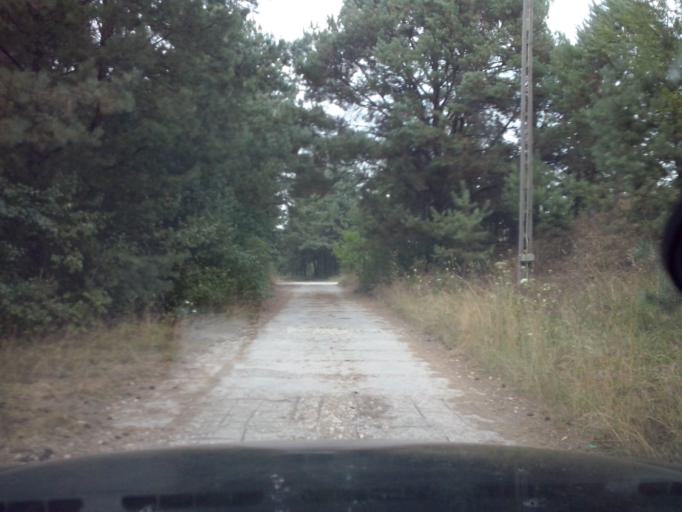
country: PL
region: Swietokrzyskie
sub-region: Powiat kielecki
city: Brzeziny
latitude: 50.7564
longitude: 20.5816
